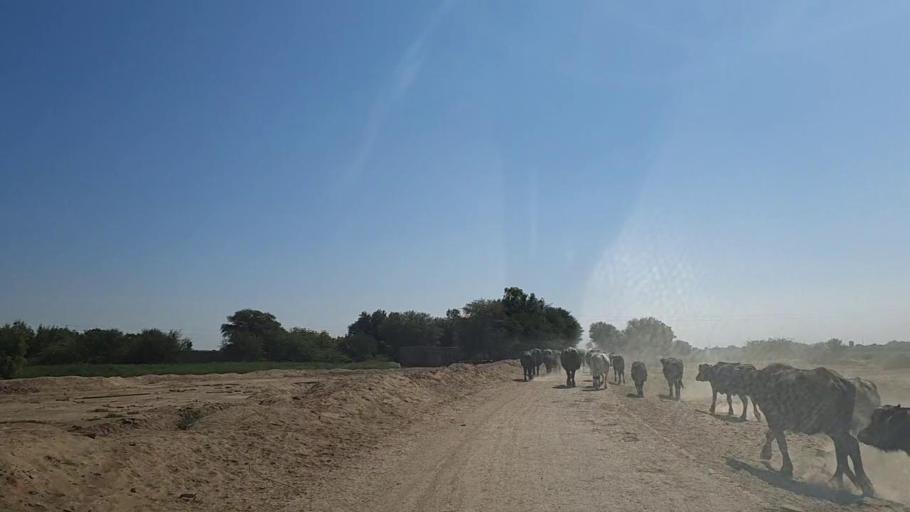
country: PK
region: Sindh
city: Dhoro Naro
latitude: 25.3597
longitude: 69.5285
